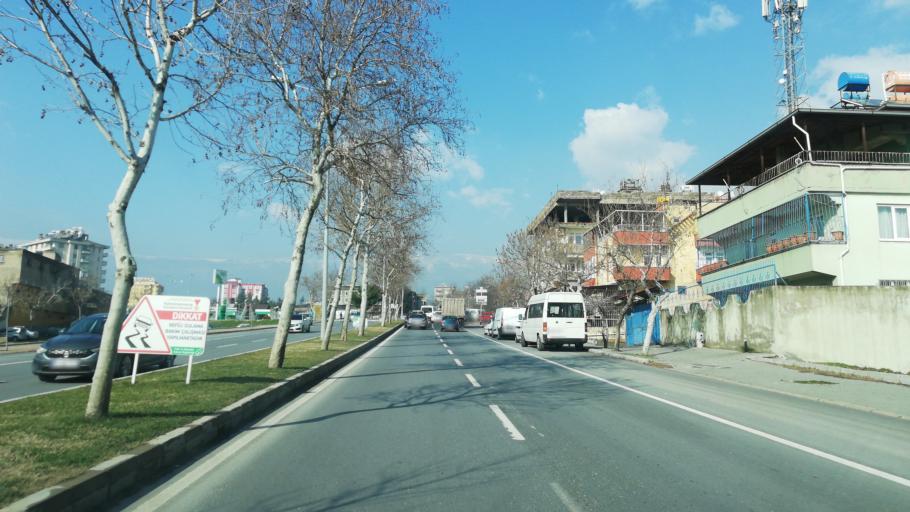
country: TR
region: Kahramanmaras
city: Kahramanmaras
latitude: 37.5700
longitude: 36.9428
